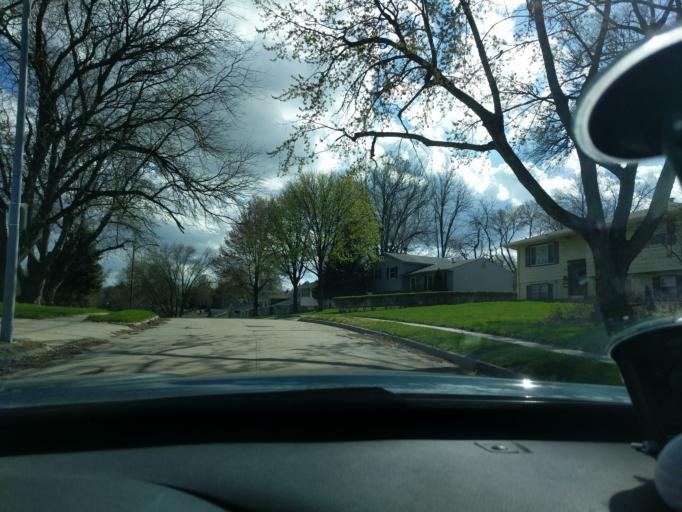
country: US
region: Nebraska
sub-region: Douglas County
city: Ralston
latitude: 41.2324
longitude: -96.0965
